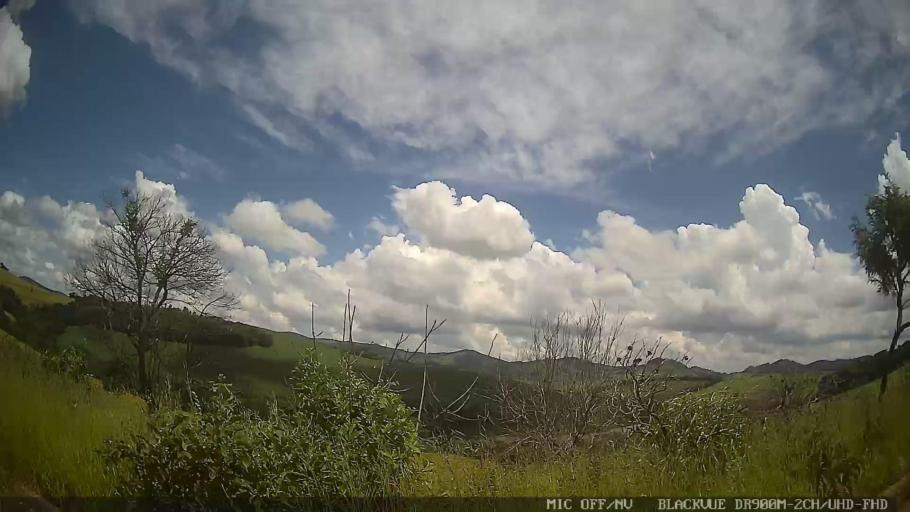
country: BR
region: Minas Gerais
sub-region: Extrema
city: Extrema
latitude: -22.7254
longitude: -46.4087
